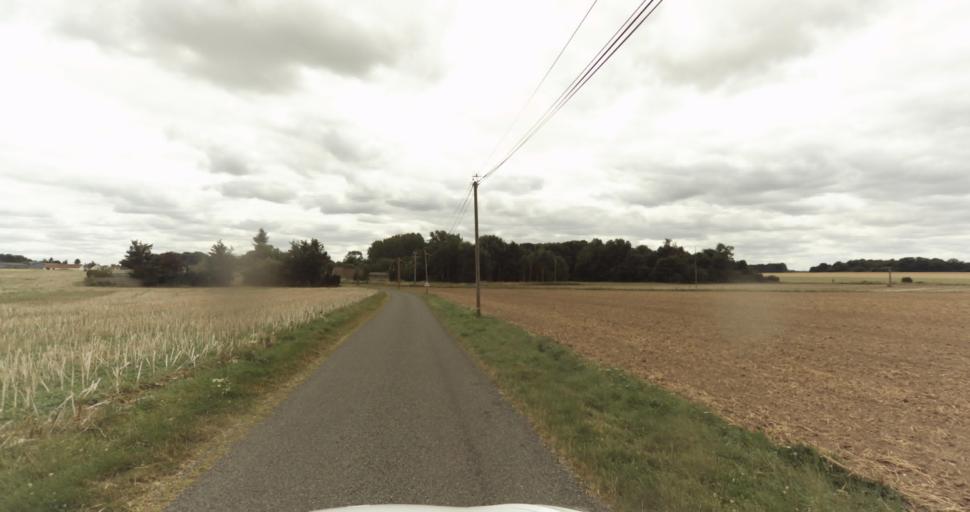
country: FR
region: Haute-Normandie
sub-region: Departement de l'Eure
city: Saint-Germain-sur-Avre
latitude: 48.8236
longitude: 1.2589
